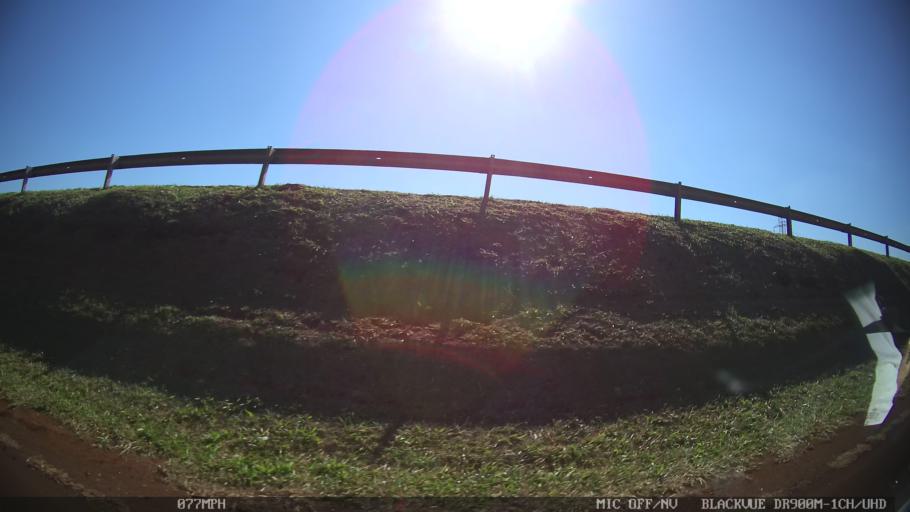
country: BR
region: Sao Paulo
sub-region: Ribeirao Preto
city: Ribeirao Preto
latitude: -21.1382
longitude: -47.8641
